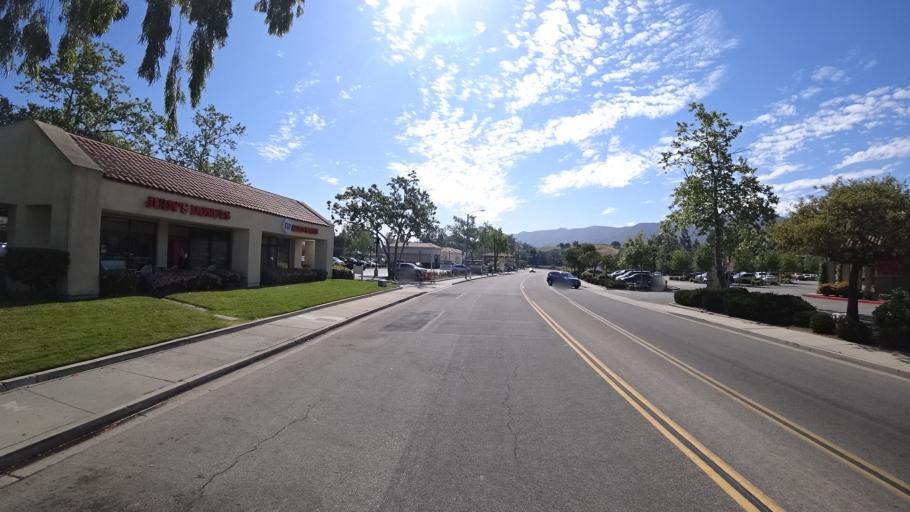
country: US
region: California
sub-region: Ventura County
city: Casa Conejo
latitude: 34.1828
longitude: -118.9288
